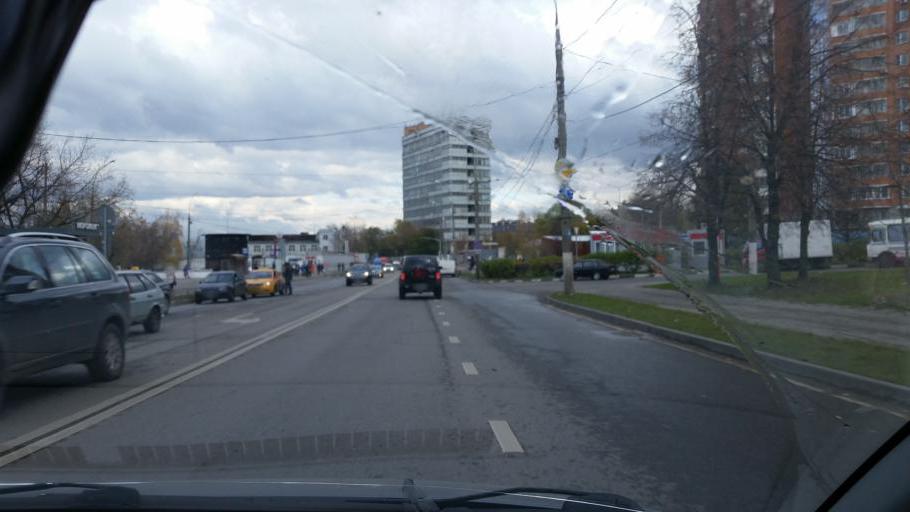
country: RU
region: Moscow
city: Kotlovka
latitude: 55.6722
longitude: 37.6096
